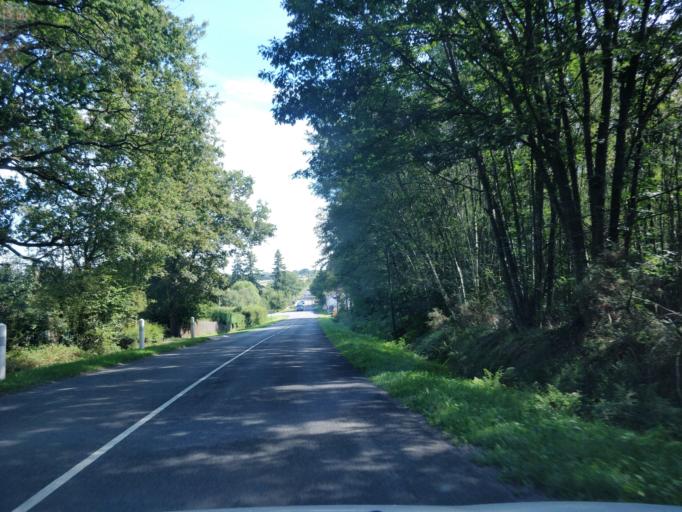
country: FR
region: Pays de la Loire
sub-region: Departement de la Loire-Atlantique
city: Quilly
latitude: 47.4829
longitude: -1.9132
